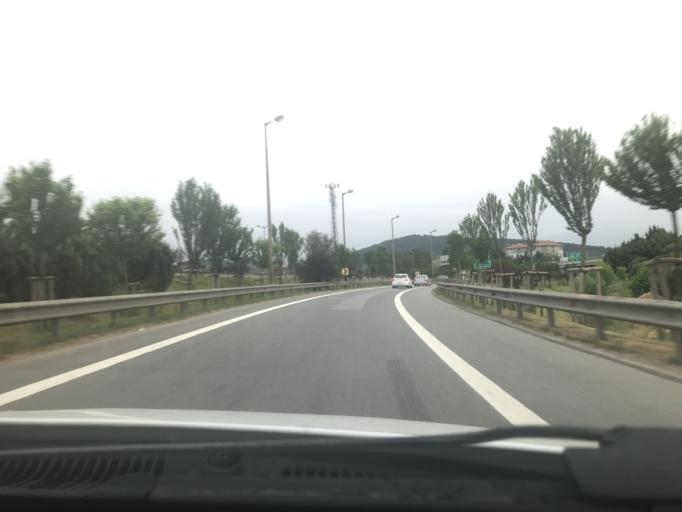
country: TR
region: Istanbul
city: Sultanbeyli
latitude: 40.9365
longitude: 29.3309
